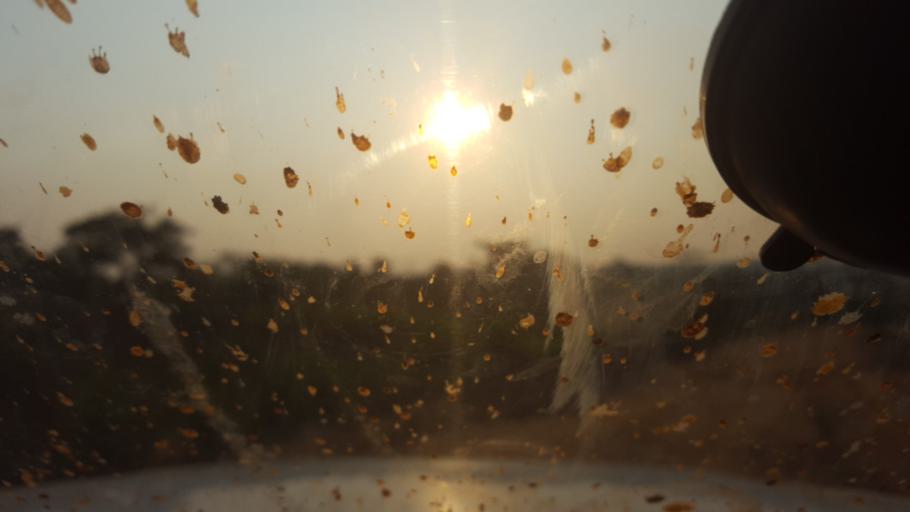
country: CD
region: Bandundu
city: Mushie
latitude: -3.7493
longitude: 16.6615
